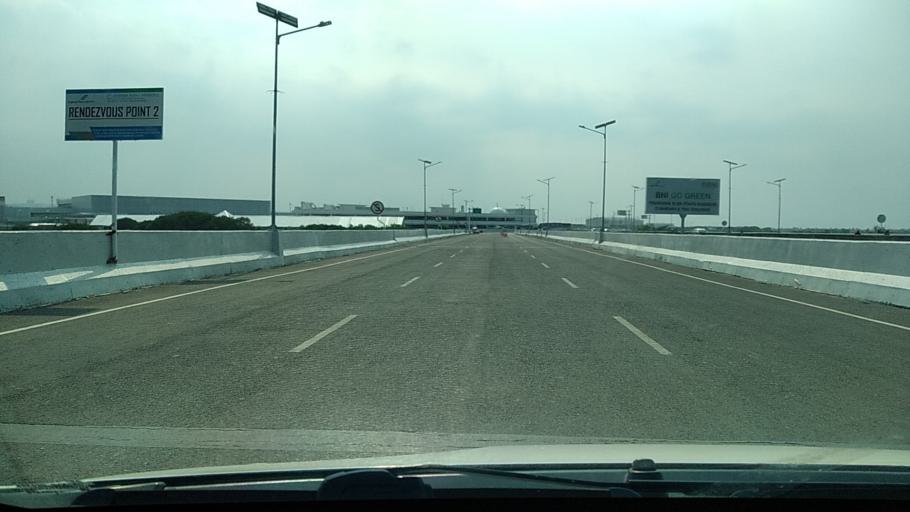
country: ID
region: Central Java
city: Semarang
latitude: -6.9639
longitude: 110.3790
